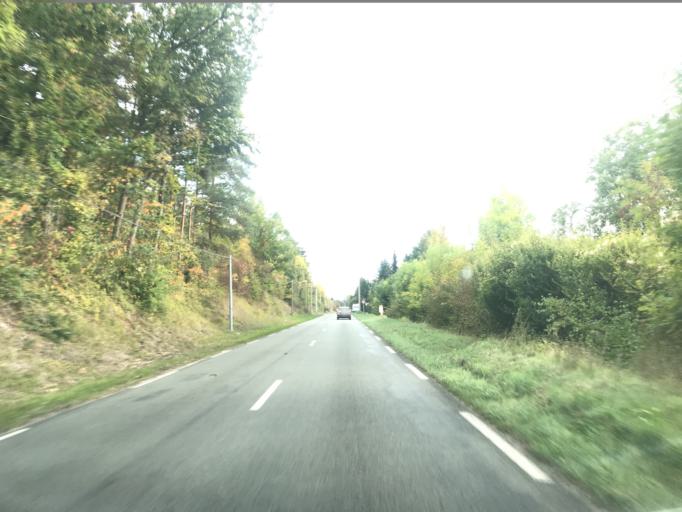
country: FR
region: Haute-Normandie
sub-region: Departement de l'Eure
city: Heudreville-sur-Eure
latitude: 49.1375
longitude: 1.2053
